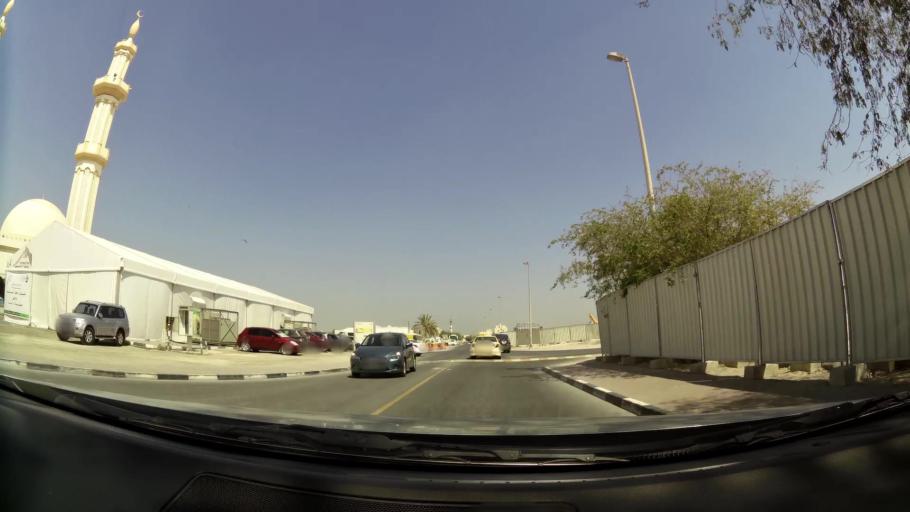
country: AE
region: Ash Shariqah
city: Sharjah
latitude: 25.2199
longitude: 55.2754
